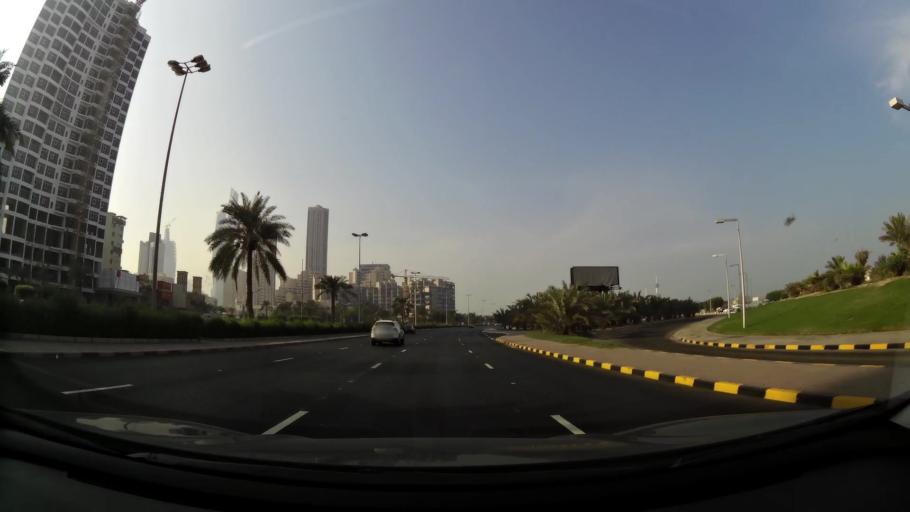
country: KW
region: Al Asimah
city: Ad Dasmah
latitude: 29.3741
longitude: 48.0061
